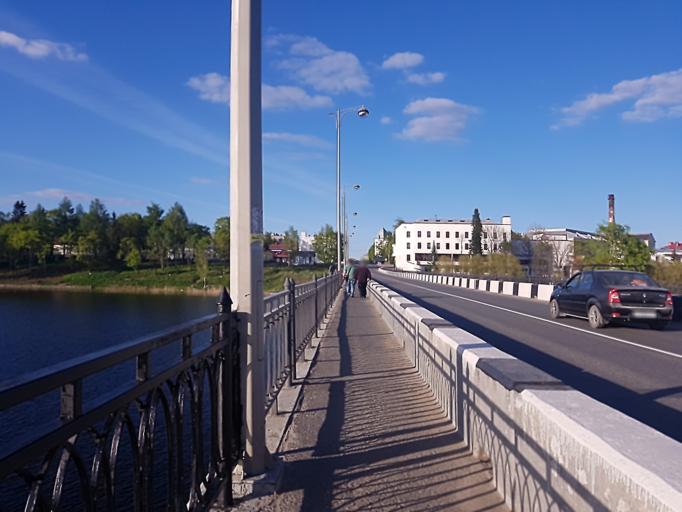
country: RU
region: Republic of Karelia
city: Sortavala
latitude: 61.7003
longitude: 30.6852
